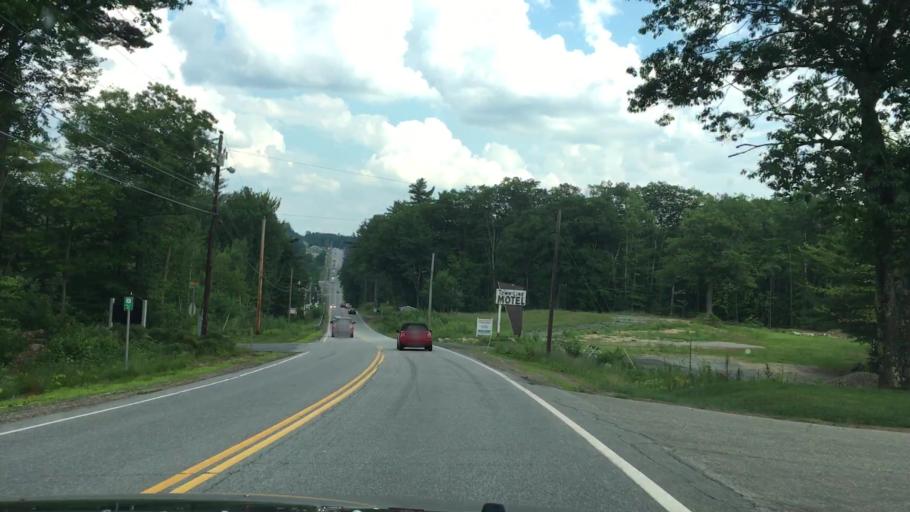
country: US
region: New Hampshire
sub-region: Belknap County
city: Meredith
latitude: 43.6234
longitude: -71.4858
